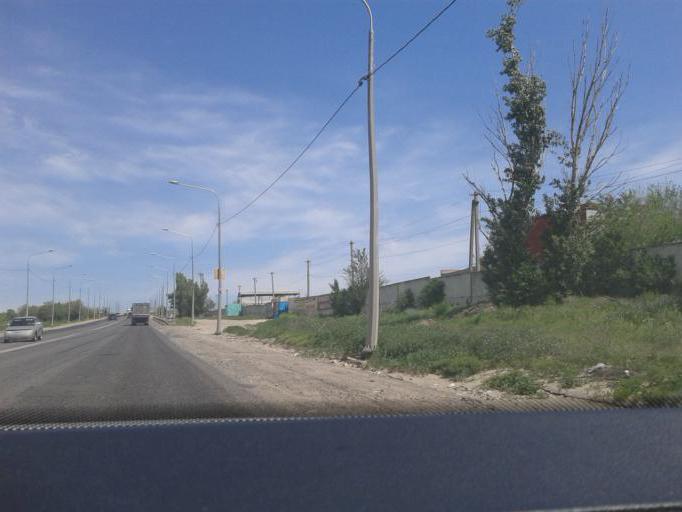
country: RU
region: Volgograd
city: Gorodishche
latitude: 48.8021
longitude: 44.5222
